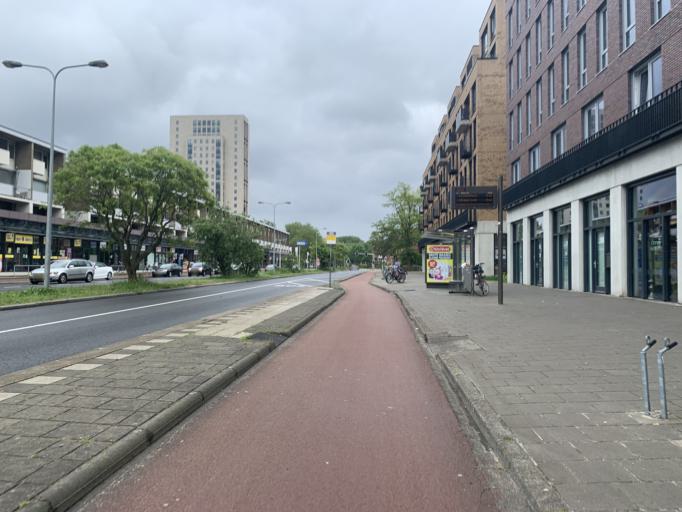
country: NL
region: Groningen
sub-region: Gemeente Groningen
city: Korrewegwijk
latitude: 53.2304
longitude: 6.5418
